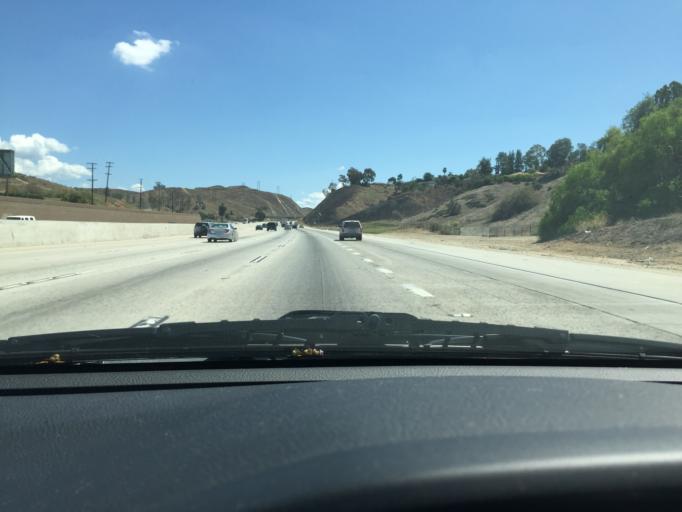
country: US
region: California
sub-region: San Bernardino County
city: Mentone
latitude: 34.0354
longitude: -117.1465
